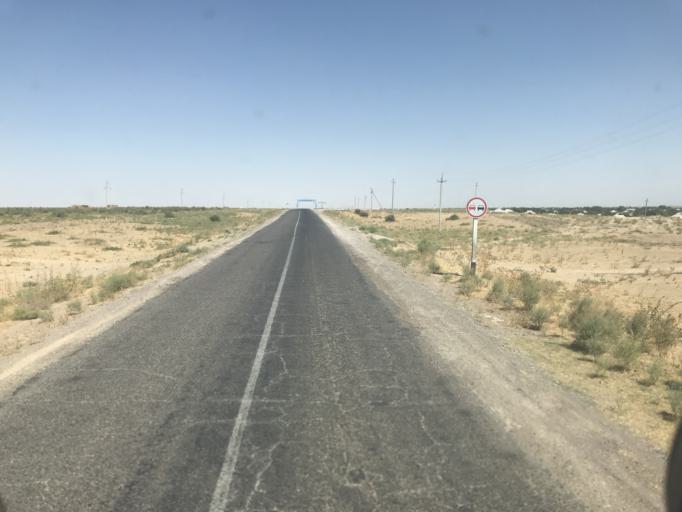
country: UZ
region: Toshkent
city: Chinoz
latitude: 41.2797
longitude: 68.6452
